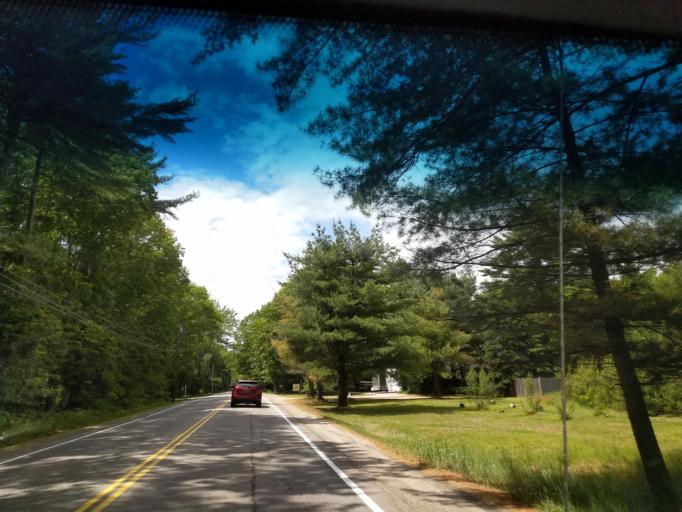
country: US
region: Maine
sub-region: Cumberland County
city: Westbrook
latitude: 43.6304
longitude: -70.3800
